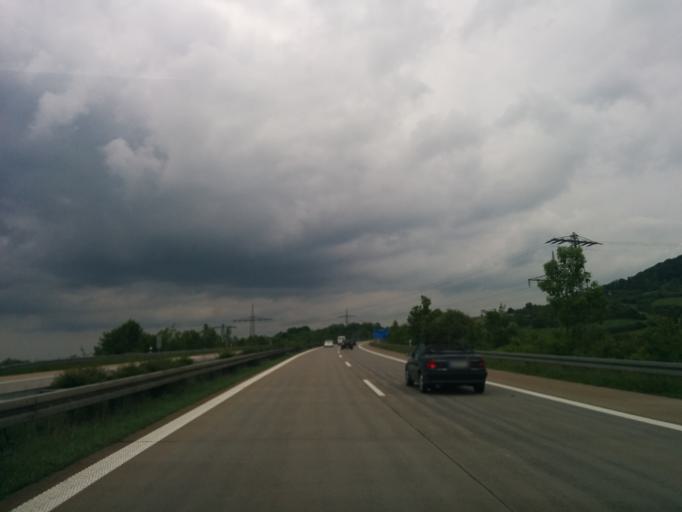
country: DE
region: Bavaria
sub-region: Regierungsbezirk Mittelfranken
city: Neusitz
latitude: 49.3798
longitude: 10.2174
